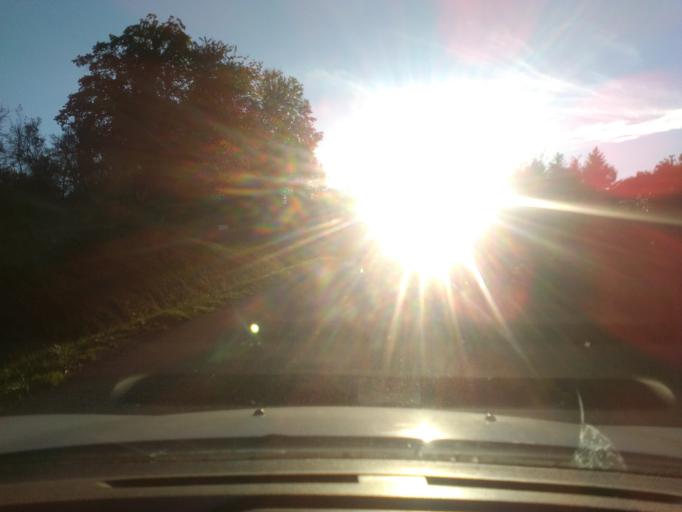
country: FR
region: Lorraine
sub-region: Departement des Vosges
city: Vincey
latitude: 48.3305
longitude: 6.3127
